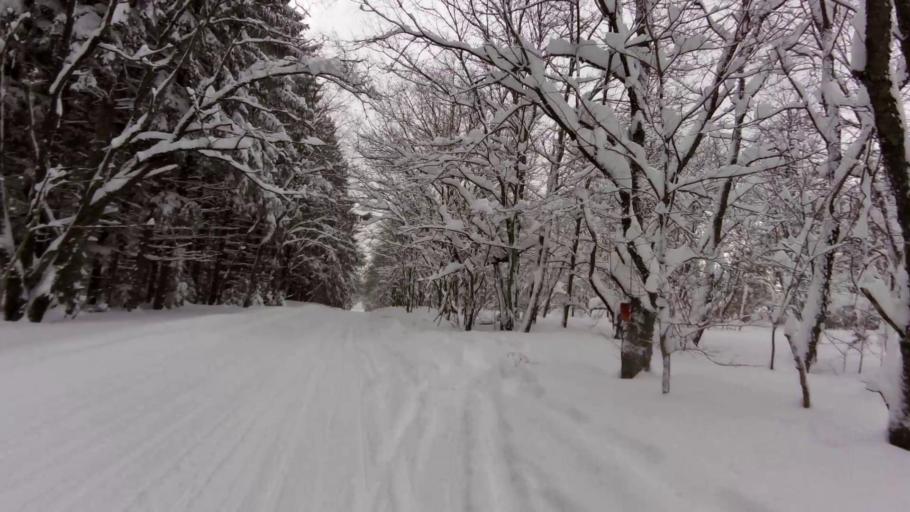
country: US
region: New York
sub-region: Lewis County
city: Lowville
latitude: 43.7325
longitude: -75.6566
